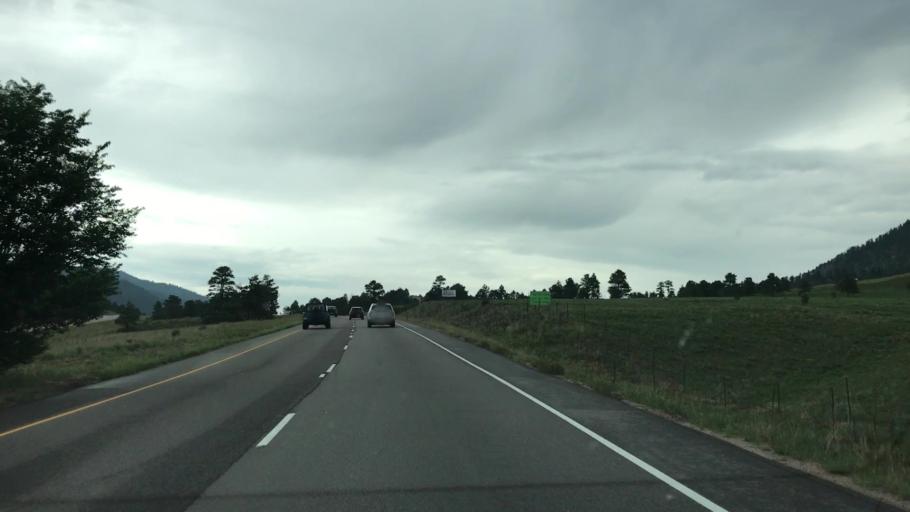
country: US
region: Colorado
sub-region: El Paso County
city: Cascade-Chipita Park
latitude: 38.9316
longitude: -105.0010
